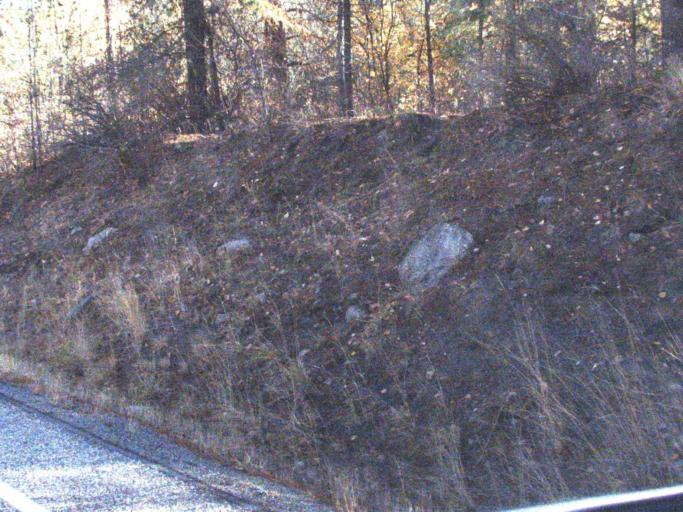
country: US
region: Washington
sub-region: Stevens County
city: Kettle Falls
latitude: 48.5856
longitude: -118.2011
